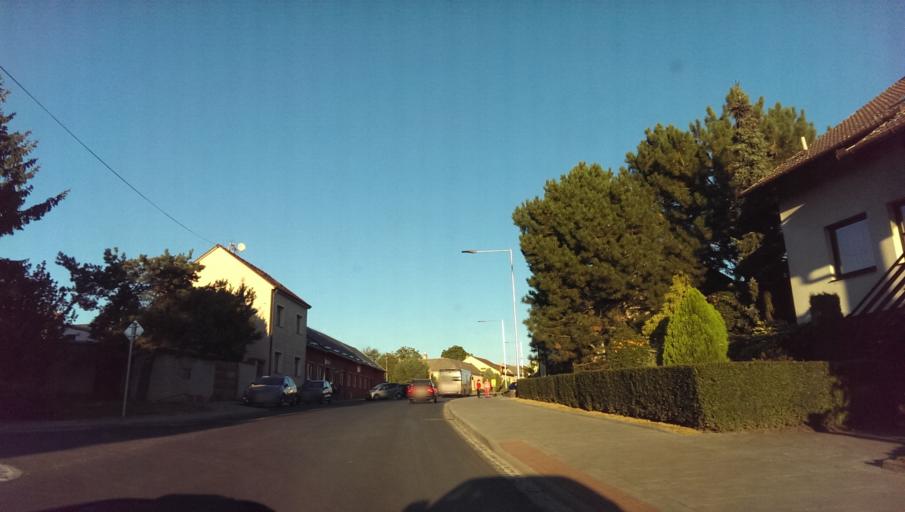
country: CZ
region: Zlin
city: Zlechov
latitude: 49.0737
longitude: 17.3847
